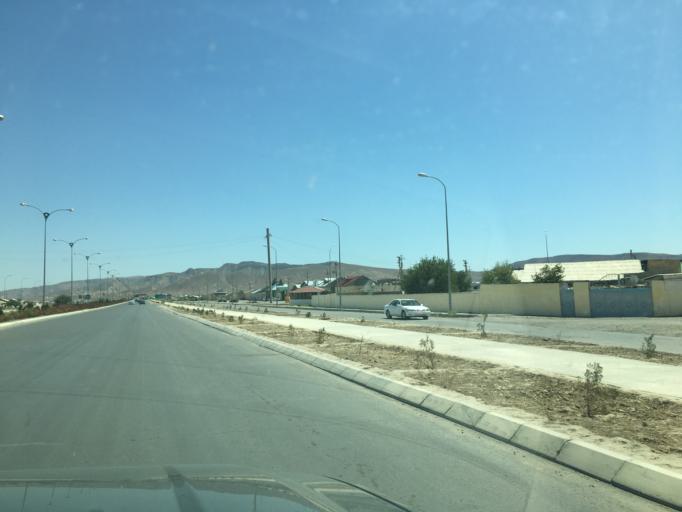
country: TM
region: Balkan
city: Serdar
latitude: 38.9890
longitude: 56.2884
